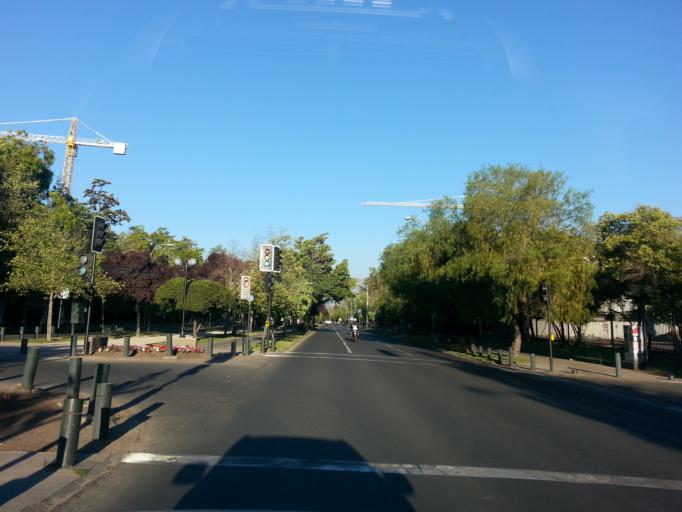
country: CL
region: Santiago Metropolitan
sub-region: Provincia de Santiago
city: Villa Presidente Frei, Nunoa, Santiago, Chile
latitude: -33.4327
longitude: -70.5939
